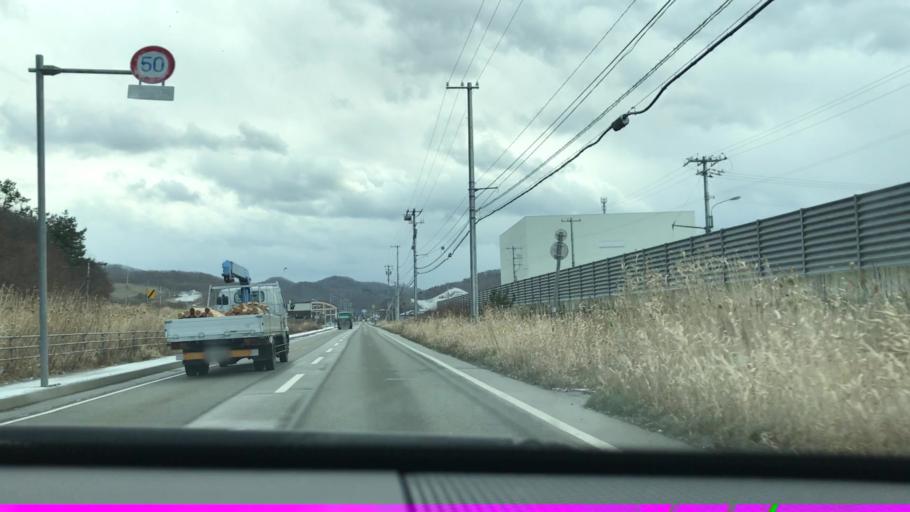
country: JP
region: Hokkaido
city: Shizunai-furukawacho
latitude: 42.3056
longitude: 142.4453
